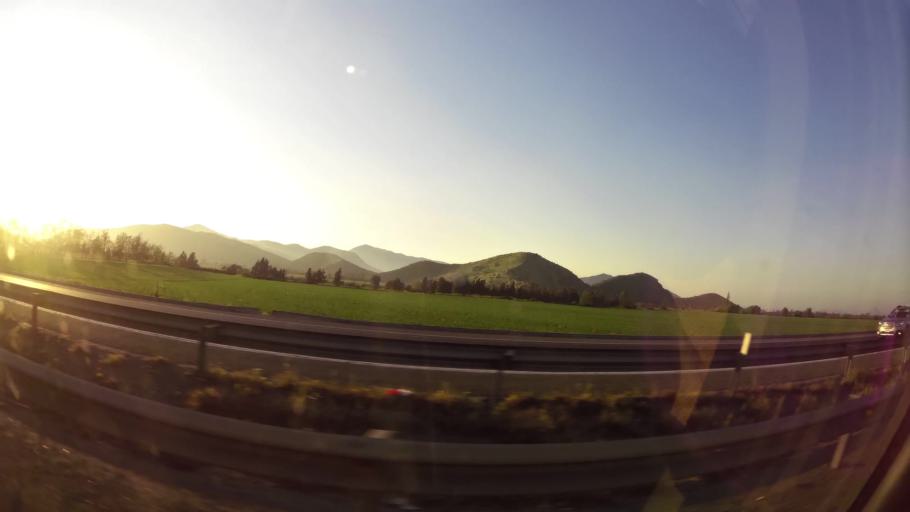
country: CL
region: Santiago Metropolitan
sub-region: Provincia de Talagante
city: Penaflor
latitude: -33.5519
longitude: -70.8122
